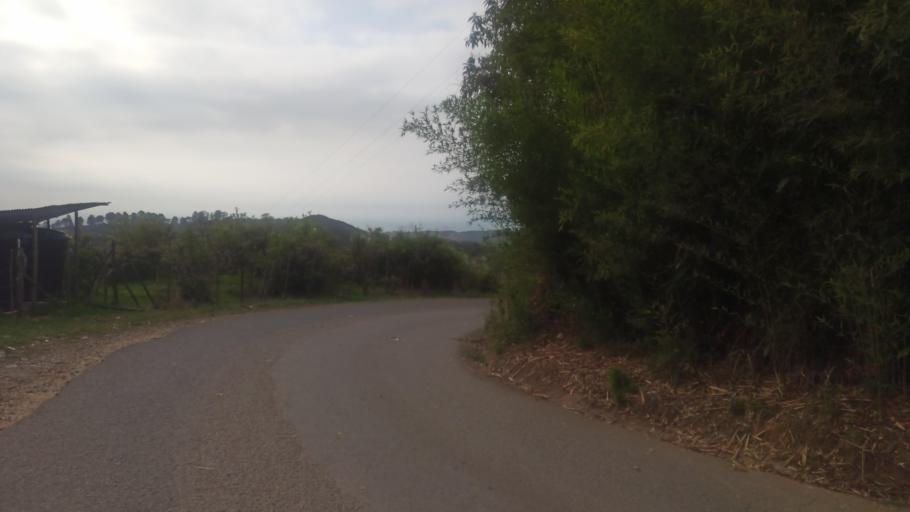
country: CO
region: Valle del Cauca
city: Jamundi
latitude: 3.2074
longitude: -76.6296
